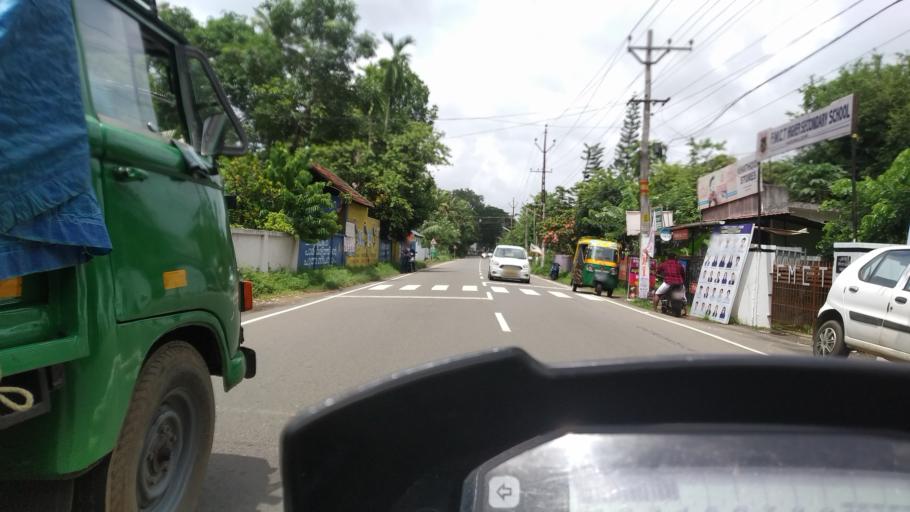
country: IN
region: Kerala
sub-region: Ernakulam
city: Elur
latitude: 10.1348
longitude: 76.2732
